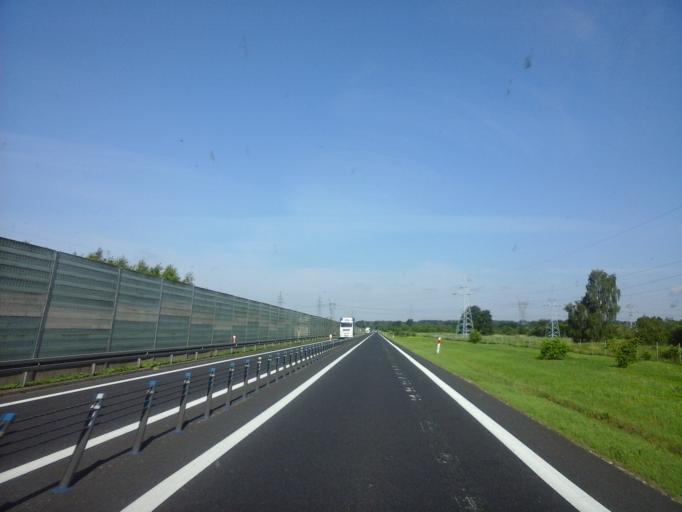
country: PL
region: West Pomeranian Voivodeship
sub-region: Powiat stargardzki
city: Kobylanka
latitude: 53.3594
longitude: 14.9165
